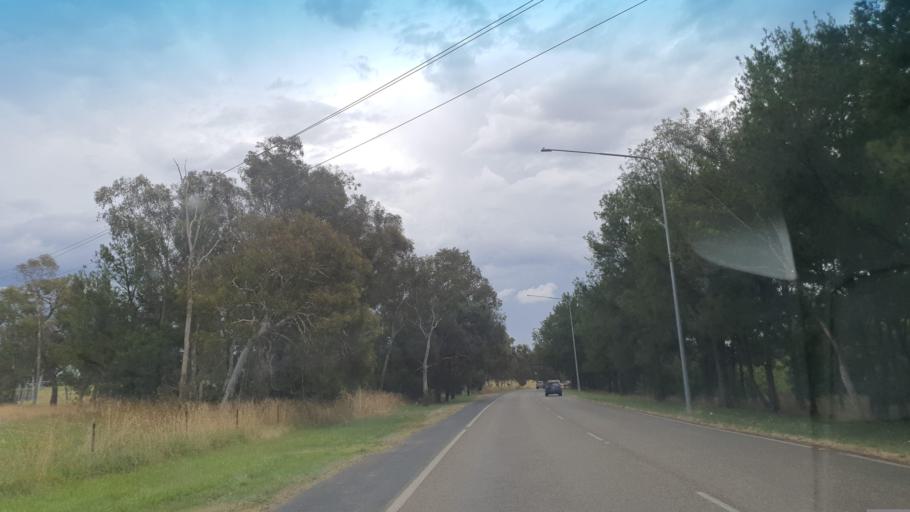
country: AU
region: Australian Capital Territory
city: Macquarie
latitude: -35.2151
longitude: 149.0396
